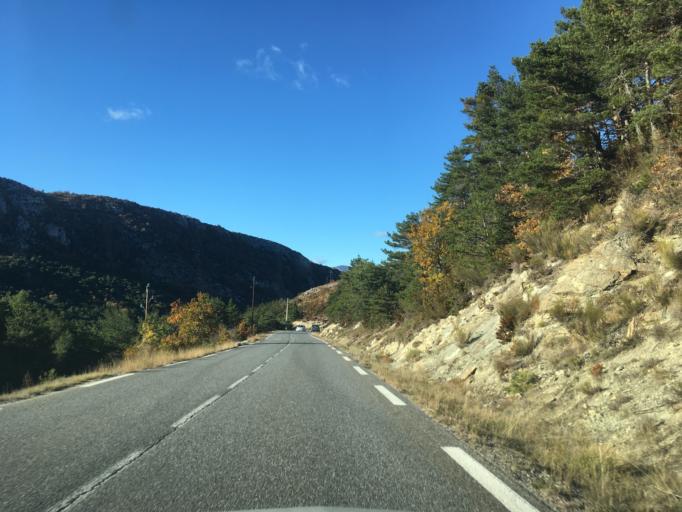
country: FR
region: Provence-Alpes-Cote d'Azur
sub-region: Departement du Var
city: Bargemon
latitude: 43.7258
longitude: 6.5048
